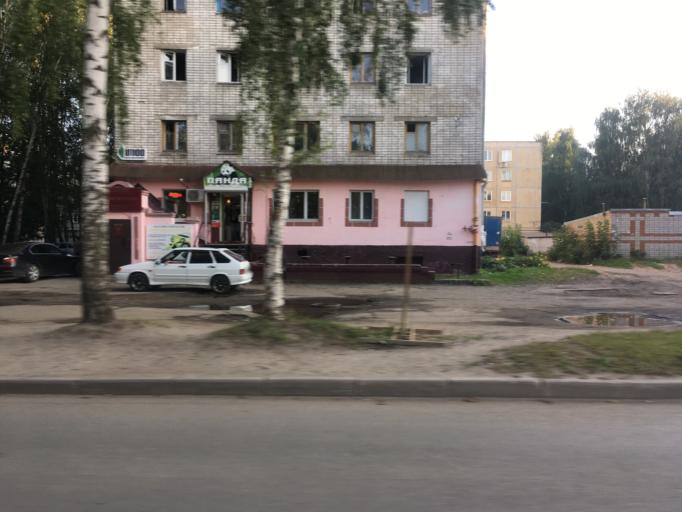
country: RU
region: Mariy-El
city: Yoshkar-Ola
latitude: 56.6486
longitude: 47.8771
